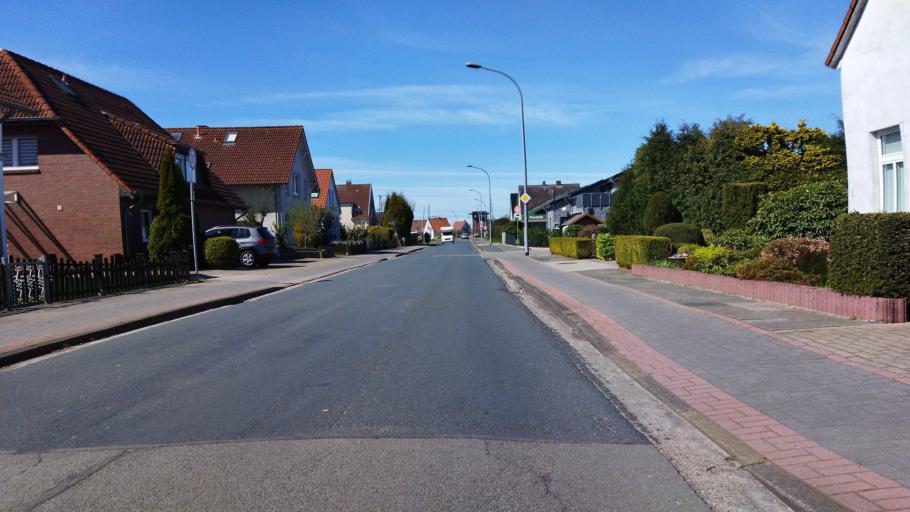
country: DE
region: Lower Saxony
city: Brake (Unterweser)
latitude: 53.3384
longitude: 8.4828
